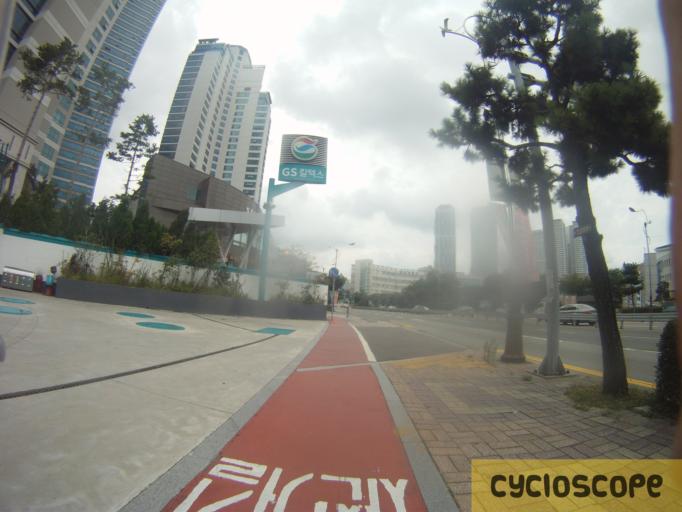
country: KR
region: Busan
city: Busan
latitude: 35.1629
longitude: 129.1347
